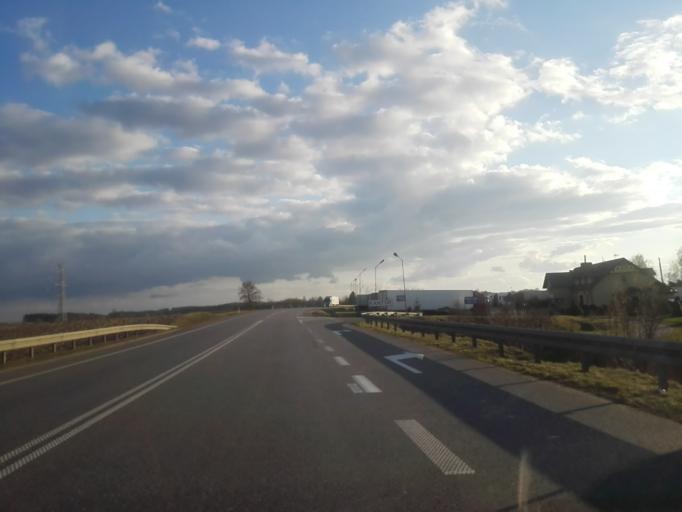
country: PL
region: Podlasie
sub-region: Suwalki
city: Suwalki
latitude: 54.1793
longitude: 22.9985
